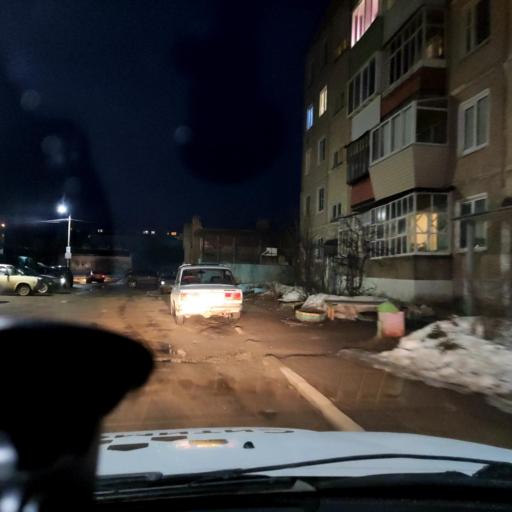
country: RU
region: Perm
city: Nytva
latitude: 57.9343
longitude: 55.3076
